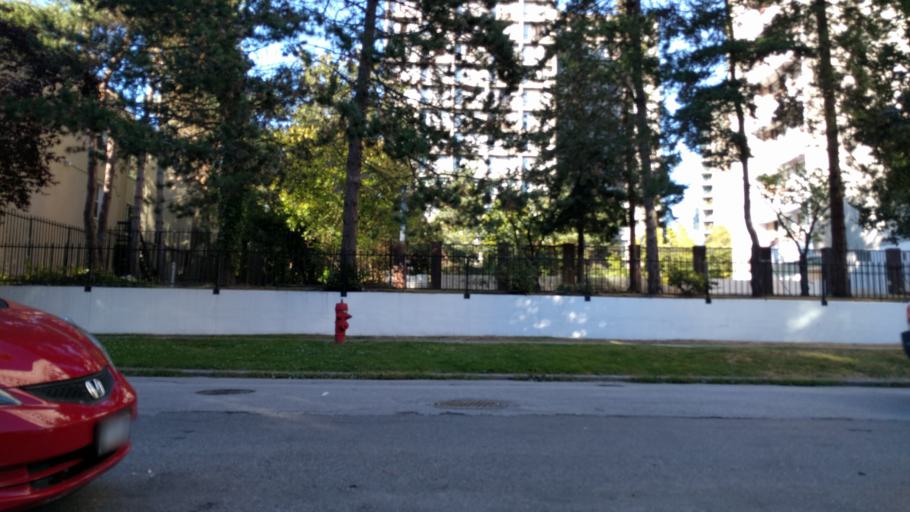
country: CA
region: British Columbia
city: West End
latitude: 49.2785
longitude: -123.1323
